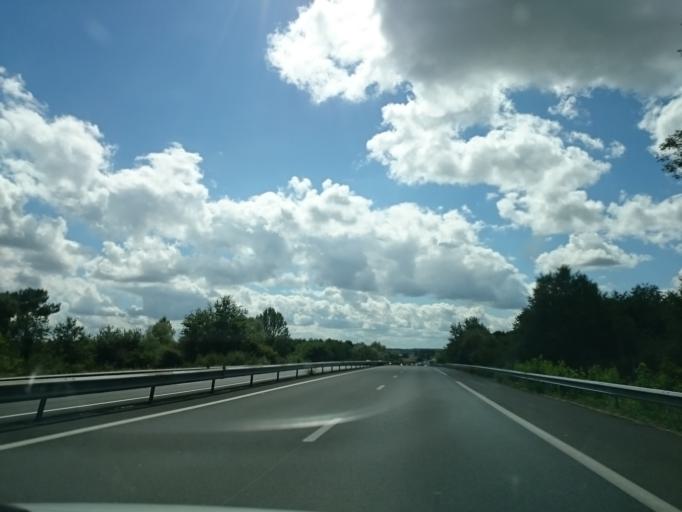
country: FR
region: Pays de la Loire
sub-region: Departement de Maine-et-Loire
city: Seiches-sur-le-Loir
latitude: 47.6046
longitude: -0.3048
